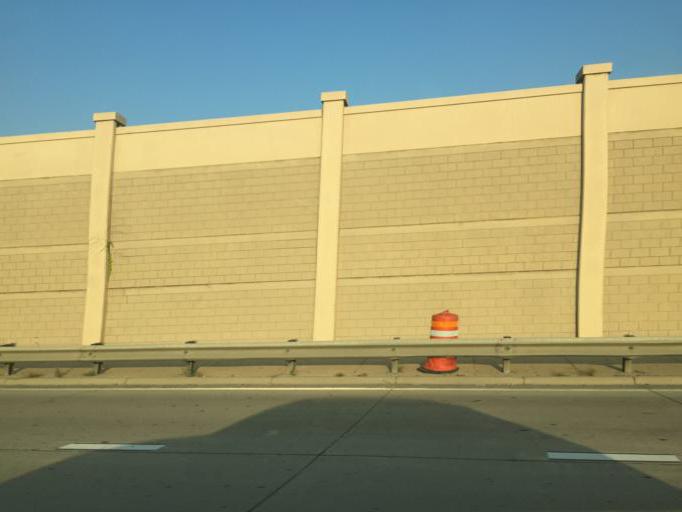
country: US
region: Minnesota
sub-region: Olmsted County
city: Rochester
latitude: 44.0344
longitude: -92.4876
